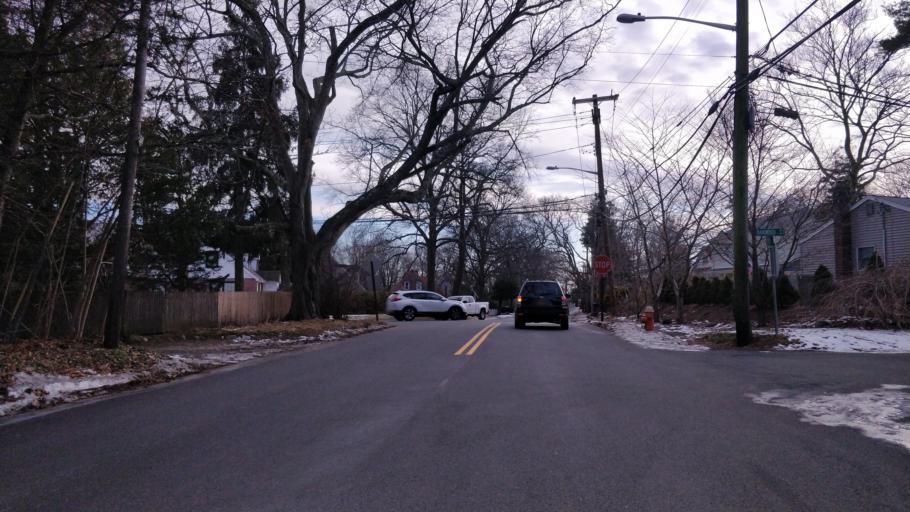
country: US
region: New York
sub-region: Suffolk County
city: Greenlawn
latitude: 40.8731
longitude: -73.3584
